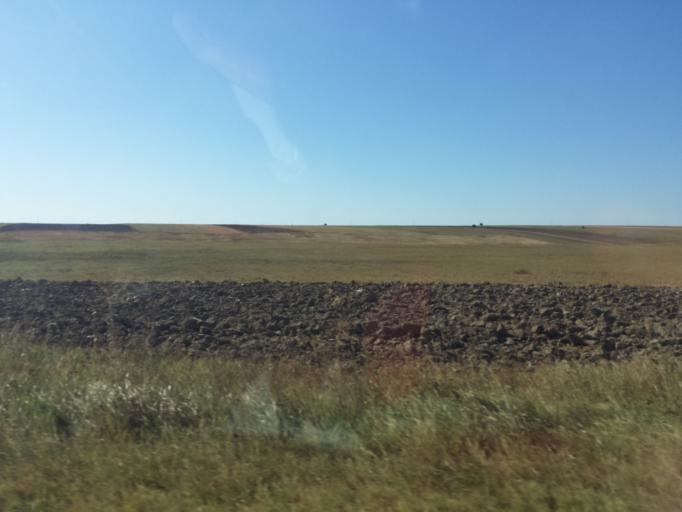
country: RO
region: Constanta
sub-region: Comuna Saraiu
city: Saraiu
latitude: 44.7341
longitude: 28.1702
